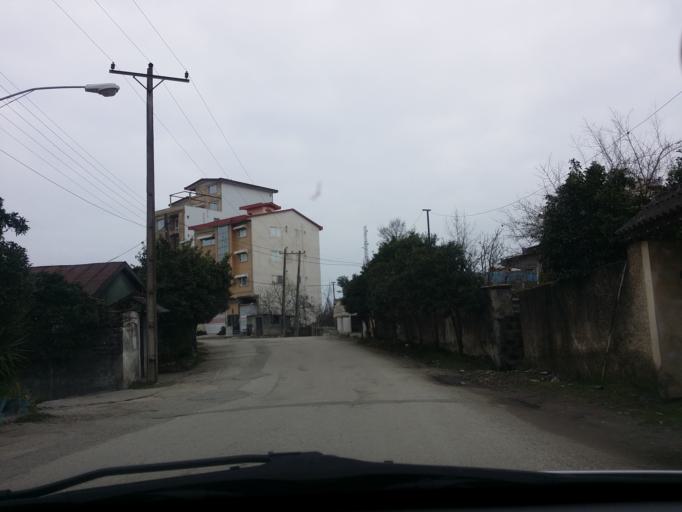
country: IR
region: Mazandaran
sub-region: Nowshahr
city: Nowshahr
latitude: 36.6546
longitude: 51.4772
